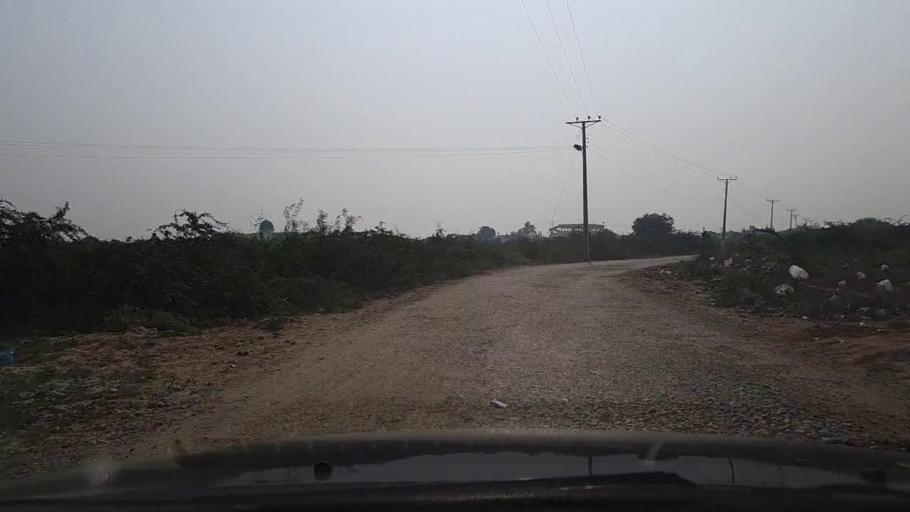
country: PK
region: Sindh
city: Thatta
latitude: 24.7492
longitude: 67.8983
